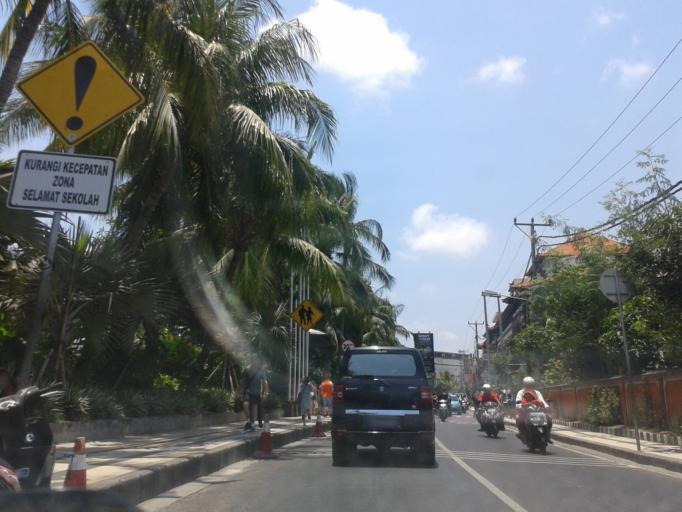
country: ID
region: Bali
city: Kuta
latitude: -8.7264
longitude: 115.1704
